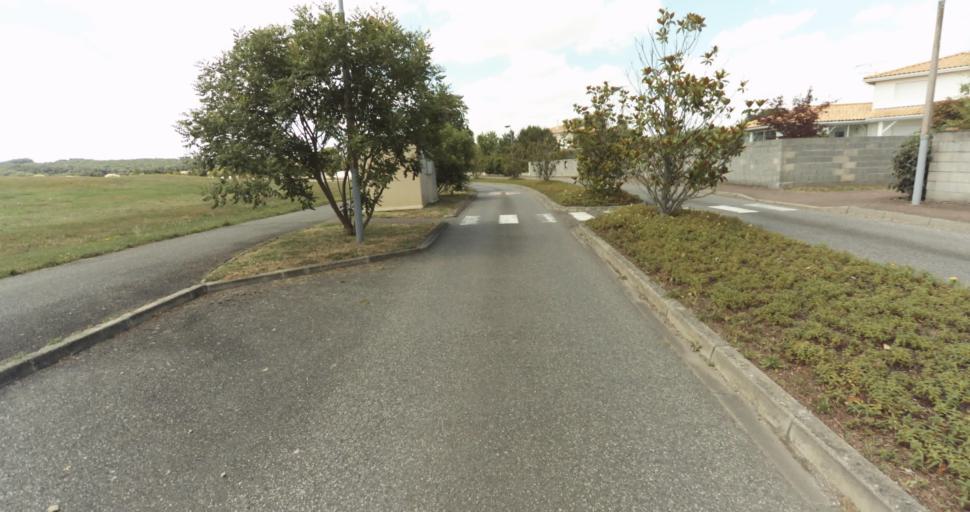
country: FR
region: Midi-Pyrenees
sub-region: Departement de la Haute-Garonne
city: Fontenilles
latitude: 43.5541
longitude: 1.1745
